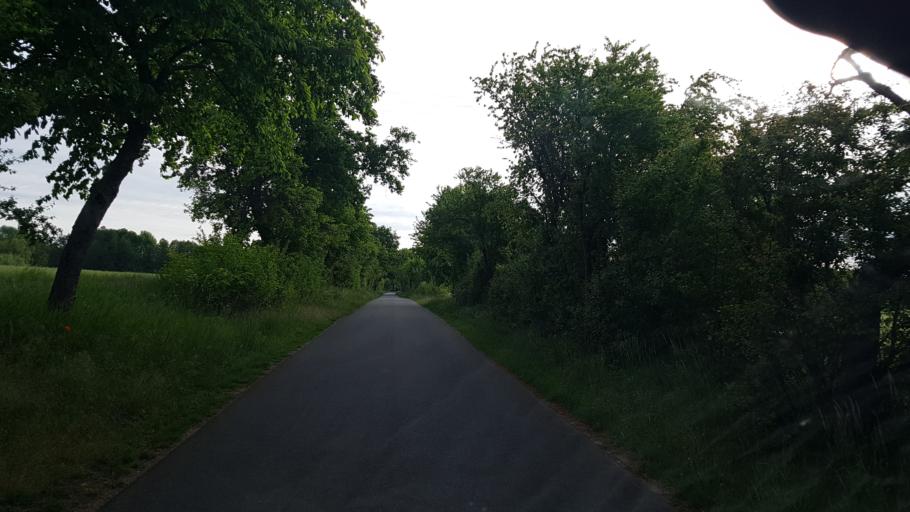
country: DE
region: Brandenburg
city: Luckau
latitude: 51.8164
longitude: 13.6428
